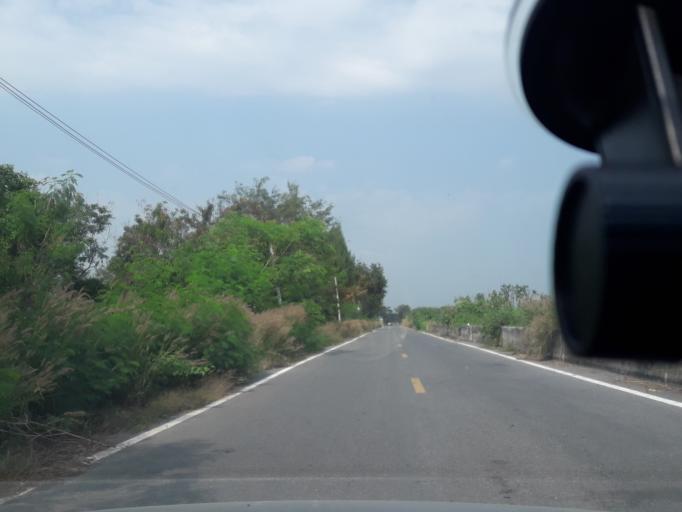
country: TH
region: Sara Buri
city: Nong Khae
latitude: 14.2713
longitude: 100.8912
